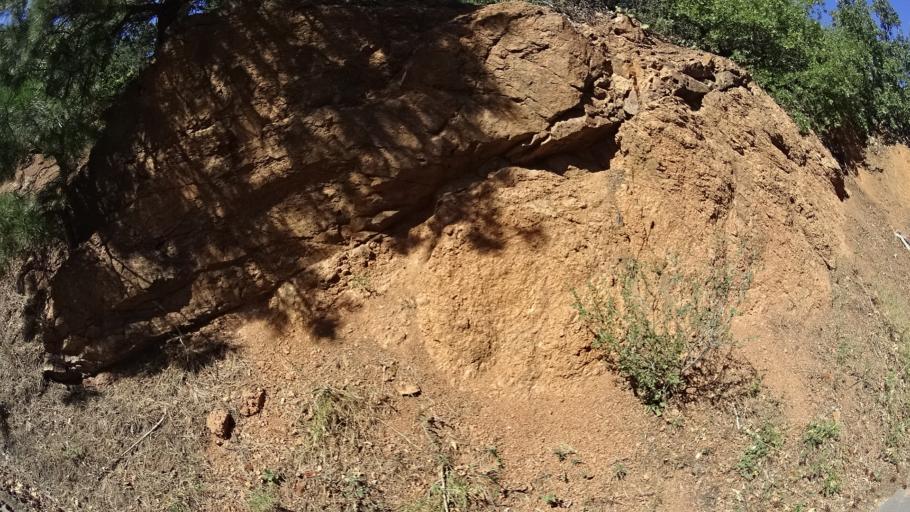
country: US
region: Colorado
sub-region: El Paso County
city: Colorado Springs
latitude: 38.8033
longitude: -104.8775
